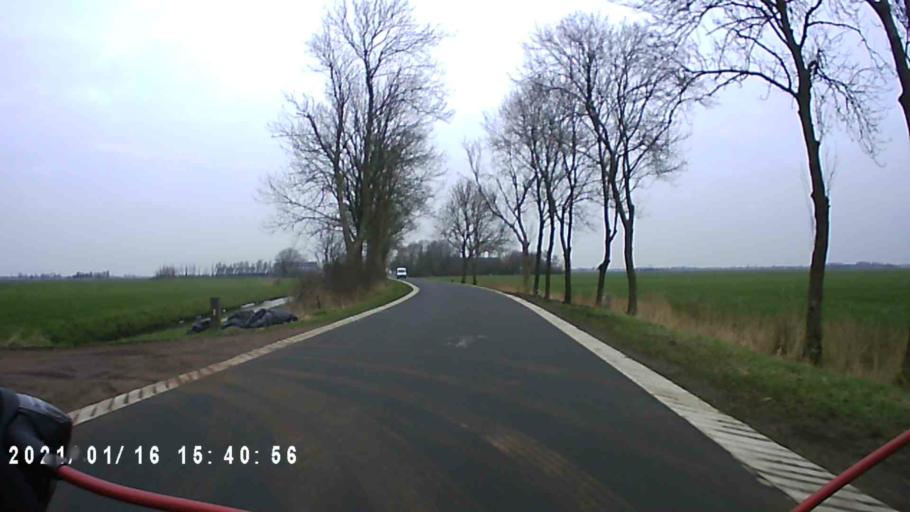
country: NL
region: Groningen
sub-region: Gemeente Groningen
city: Korrewegwijk
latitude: 53.2729
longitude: 6.5651
